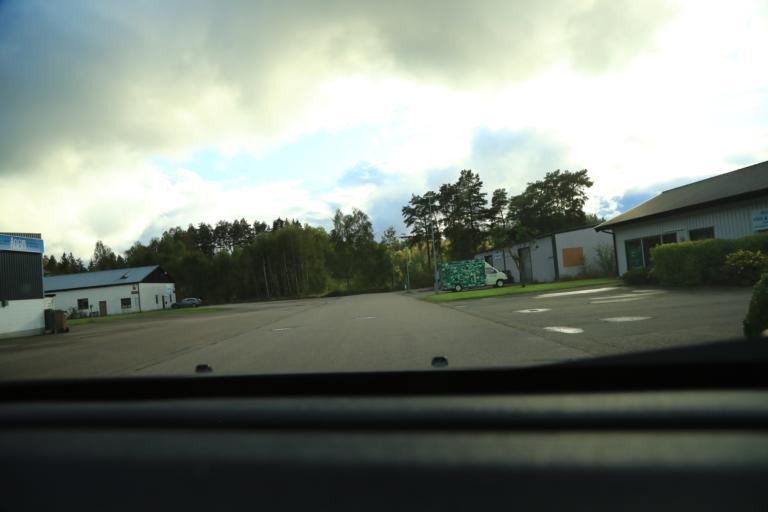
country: SE
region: Halland
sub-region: Halmstads Kommun
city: Getinge
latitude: 57.1239
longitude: 12.7117
